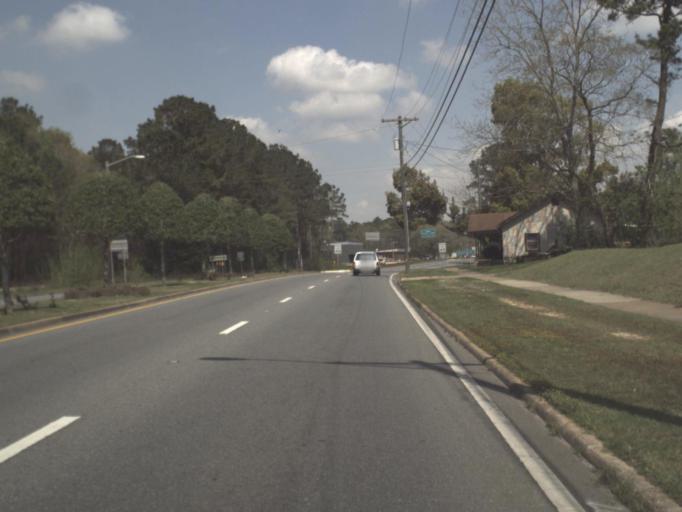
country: US
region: Florida
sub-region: Gadsden County
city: Havana
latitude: 30.6343
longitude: -84.4168
